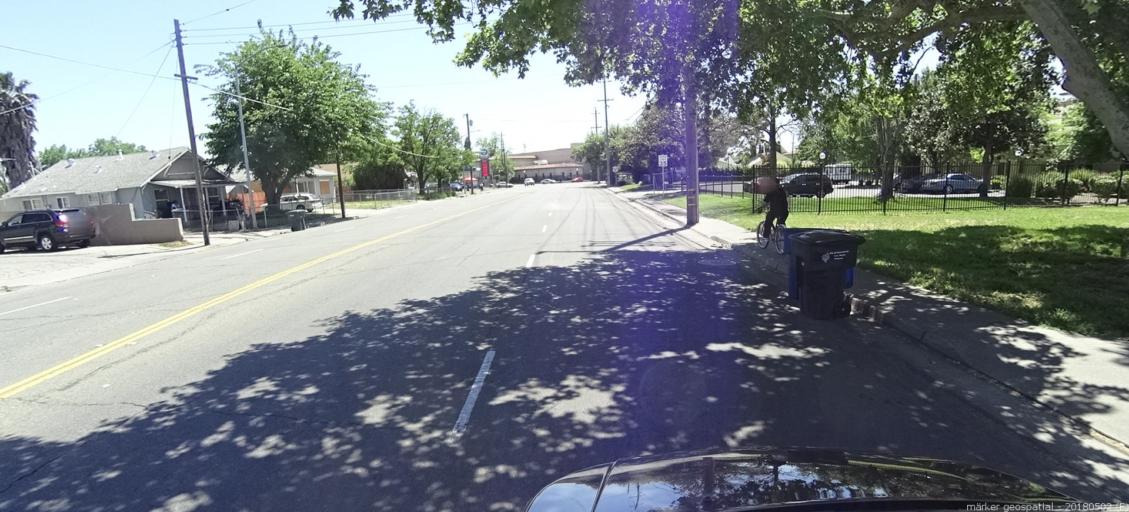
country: US
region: California
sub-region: Sacramento County
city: Sacramento
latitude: 38.6163
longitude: -121.4463
